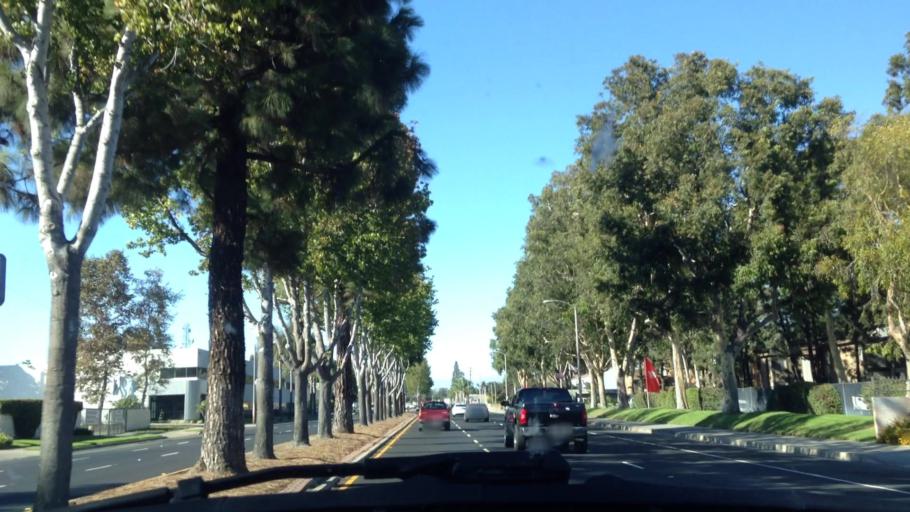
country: US
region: California
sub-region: Orange County
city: Fountain Valley
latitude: 33.7101
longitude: -117.9078
